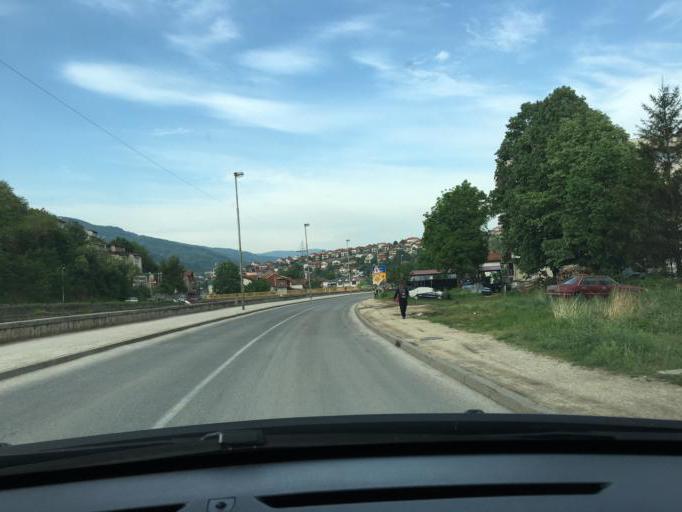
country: MK
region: Kriva Palanka
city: Kriva Palanka
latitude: 42.2091
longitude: 22.3398
